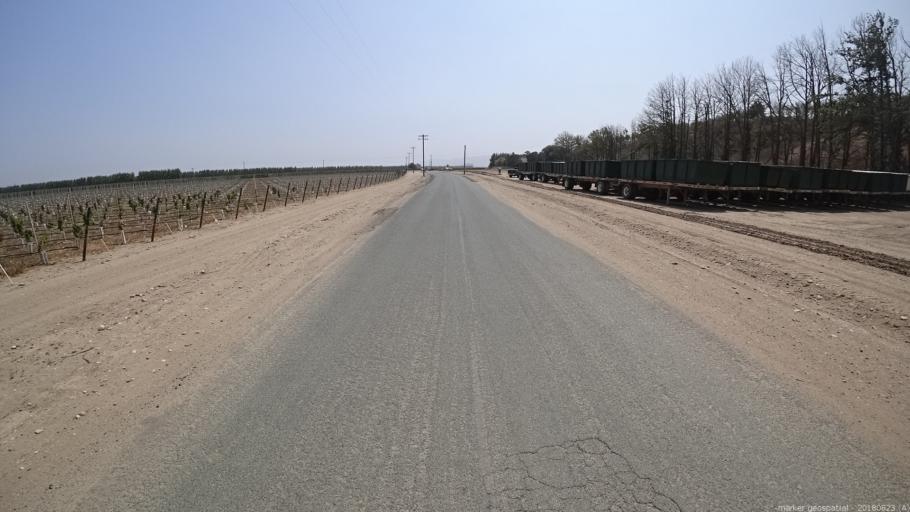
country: US
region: California
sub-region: Monterey County
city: Soledad
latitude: 36.3582
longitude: -121.3051
